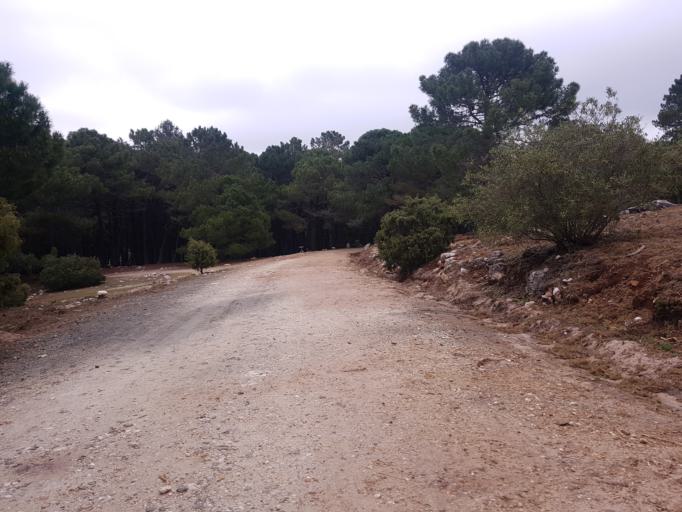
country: ES
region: Andalusia
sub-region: Provincia de Malaga
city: Ojen
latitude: 36.5670
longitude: -4.8912
